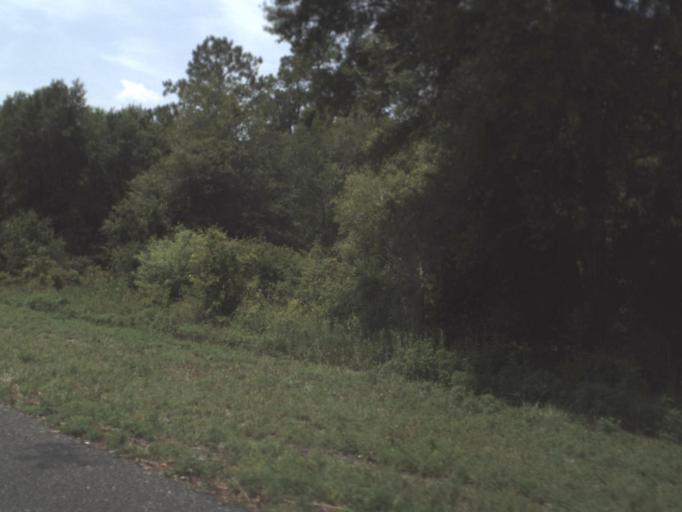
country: US
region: Florida
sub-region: Taylor County
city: Perry
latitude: 30.0431
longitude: -83.5494
